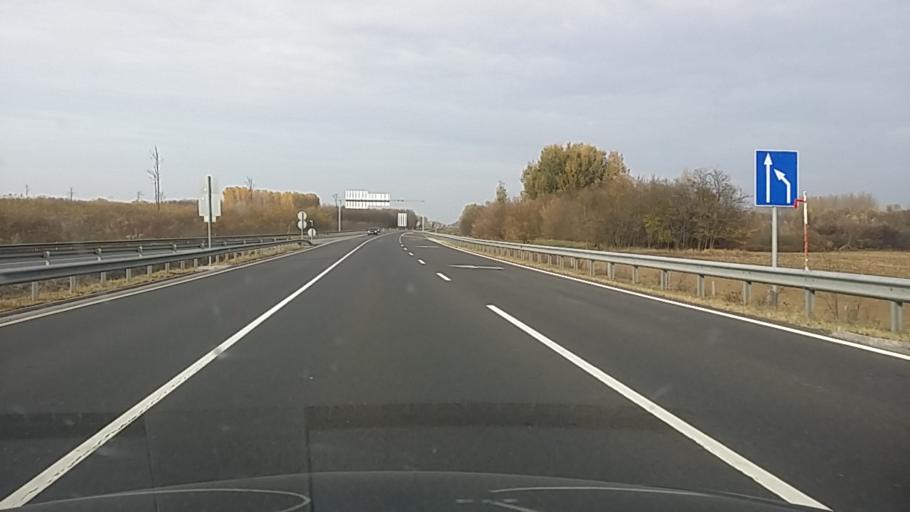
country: HU
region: Szabolcs-Szatmar-Bereg
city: Nagykallo
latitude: 47.9001
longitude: 21.8173
